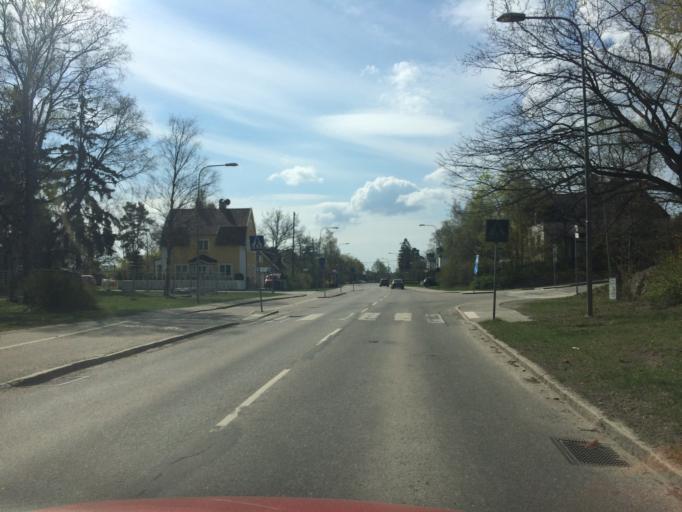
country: SE
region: Stockholm
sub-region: Huddinge Kommun
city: Segeltorp
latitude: 59.2951
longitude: 17.9549
